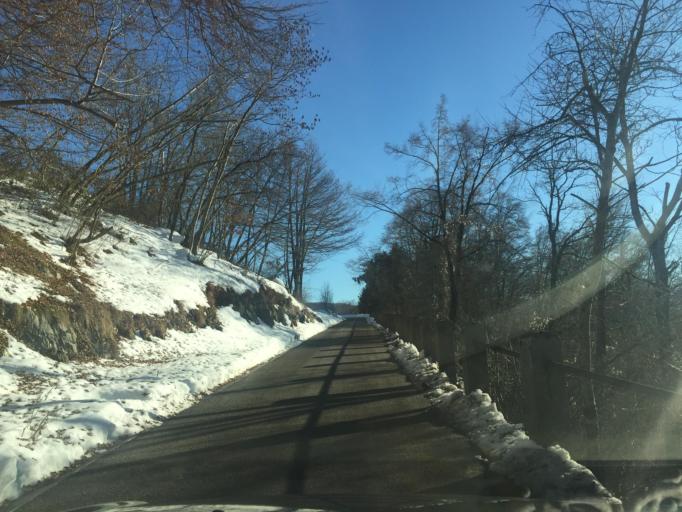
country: IT
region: Friuli Venezia Giulia
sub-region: Provincia di Udine
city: Lauco
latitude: 46.4321
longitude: 12.9706
